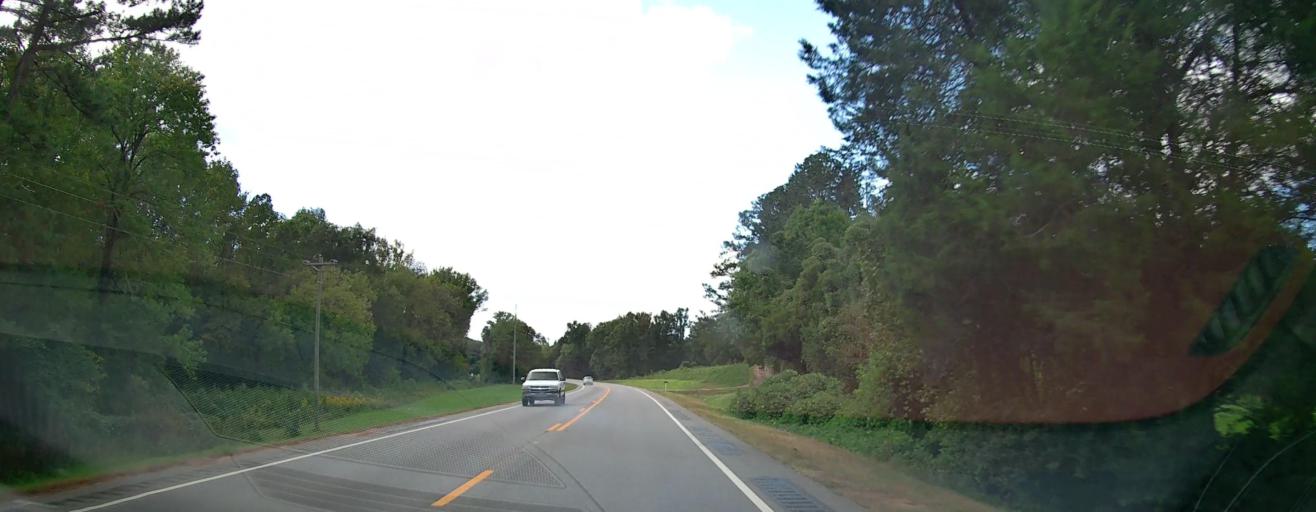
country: US
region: Georgia
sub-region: Baldwin County
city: Milledgeville
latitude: 33.0745
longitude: -83.3290
